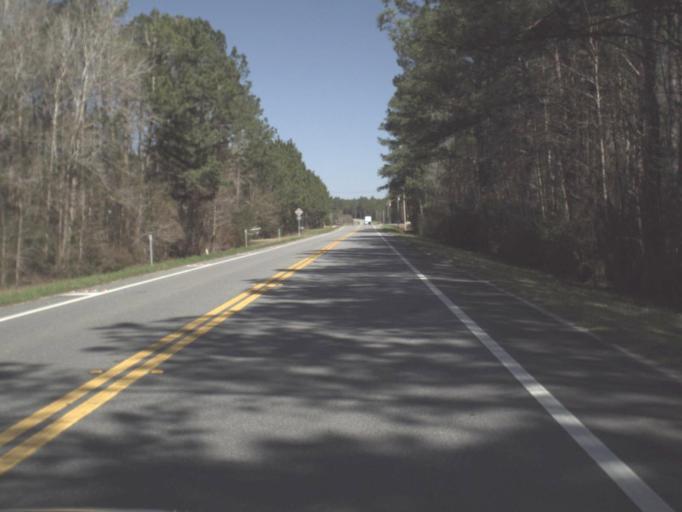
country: US
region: Florida
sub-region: Calhoun County
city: Blountstown
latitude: 30.2893
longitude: -85.1413
